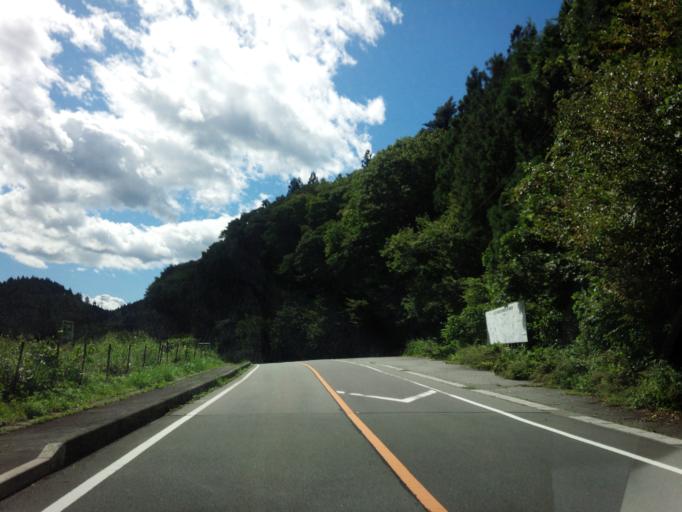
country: JP
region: Gunma
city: Nakanojomachi
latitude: 36.6557
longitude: 138.7986
